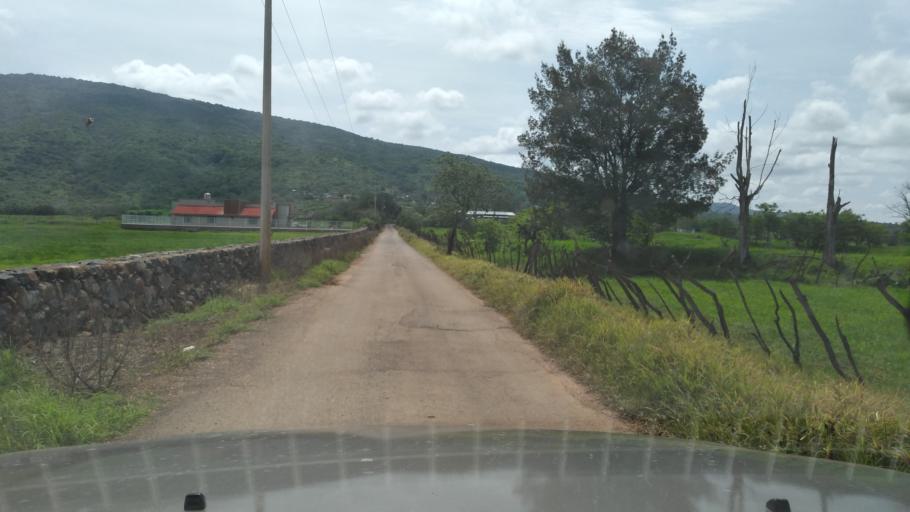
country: MX
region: Jalisco
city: Capilla de Guadalupe
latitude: 20.7494
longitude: -102.6317
